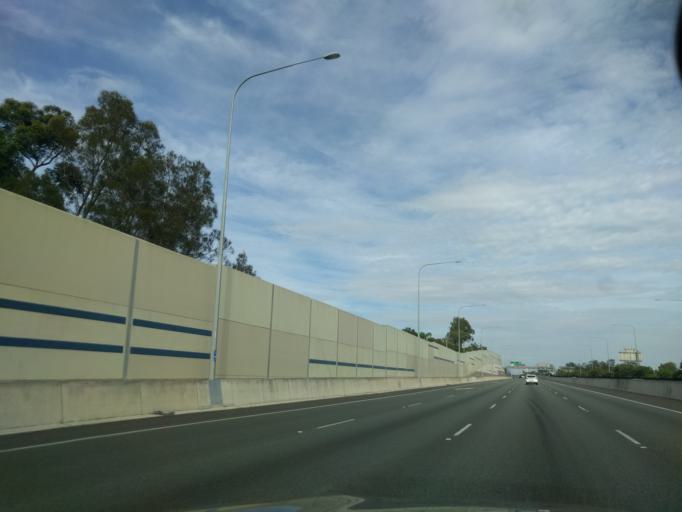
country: AU
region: Queensland
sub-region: Ipswich
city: Goodna
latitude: -27.6048
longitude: 152.8930
